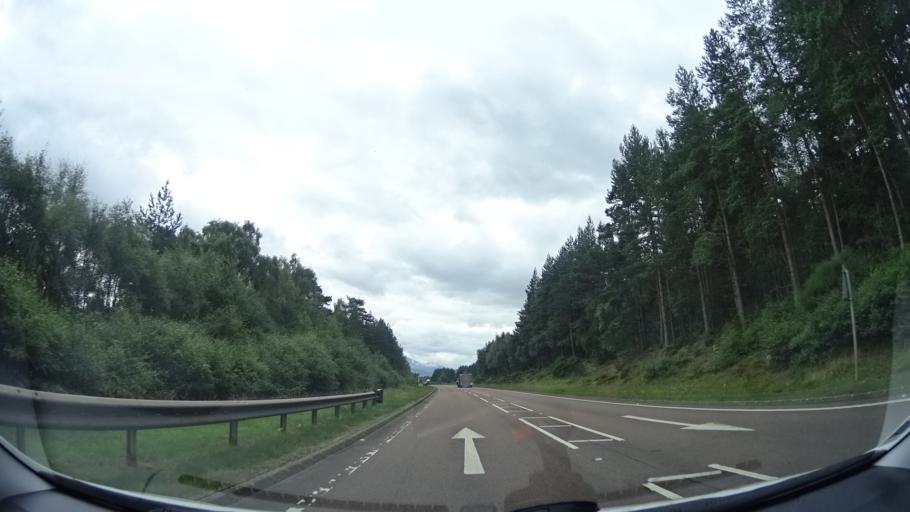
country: GB
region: Scotland
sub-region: Highland
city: Aviemore
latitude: 57.2257
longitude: -3.8195
